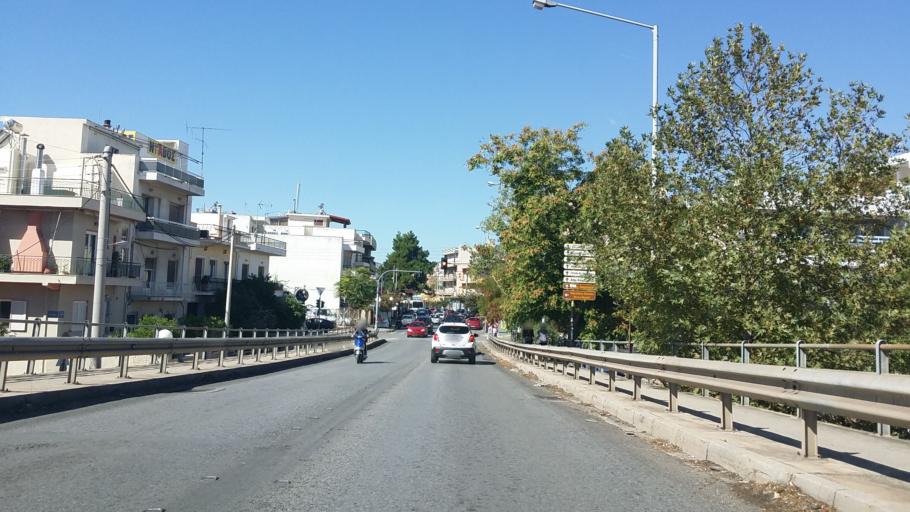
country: GR
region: Attica
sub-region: Nomarchia Athinas
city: Agioi Anargyroi
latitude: 38.0268
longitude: 23.7262
